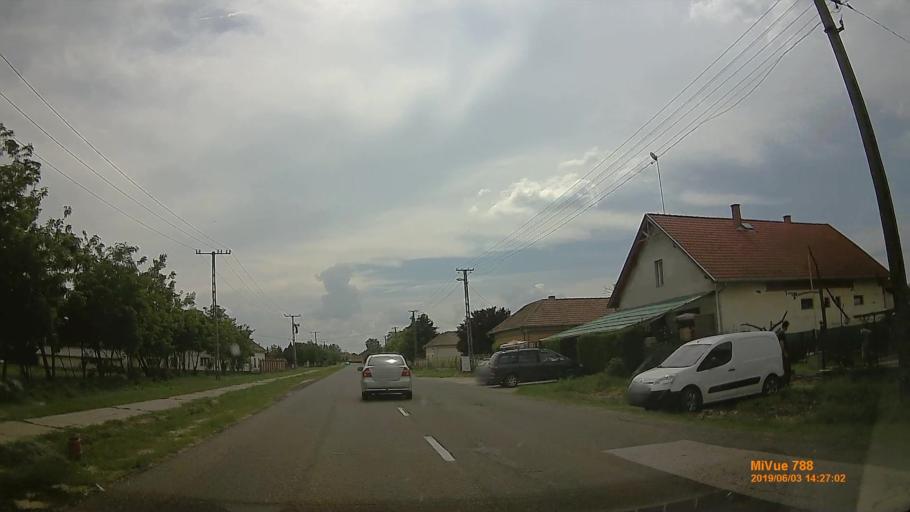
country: HU
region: Bacs-Kiskun
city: Tiszakecske
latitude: 46.9880
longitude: 20.1210
